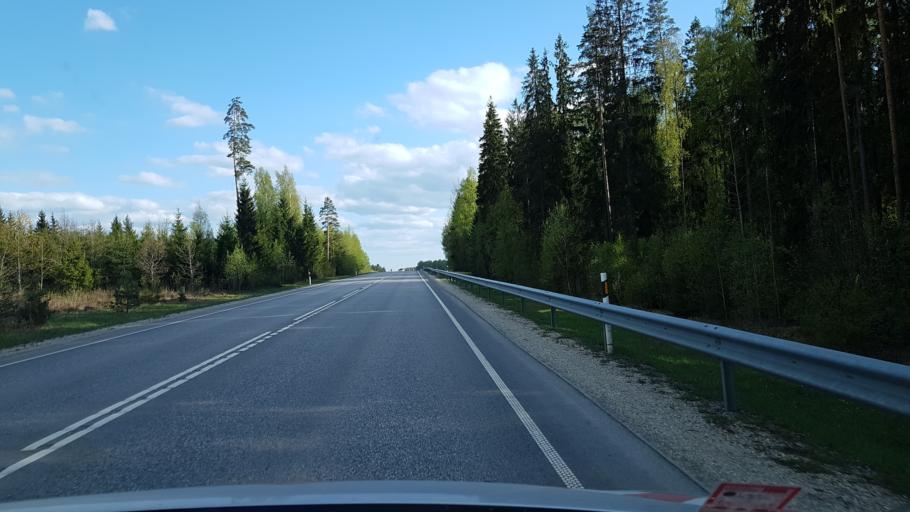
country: EE
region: Vorumaa
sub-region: Voru linn
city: Voru
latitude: 57.9391
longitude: 26.7970
